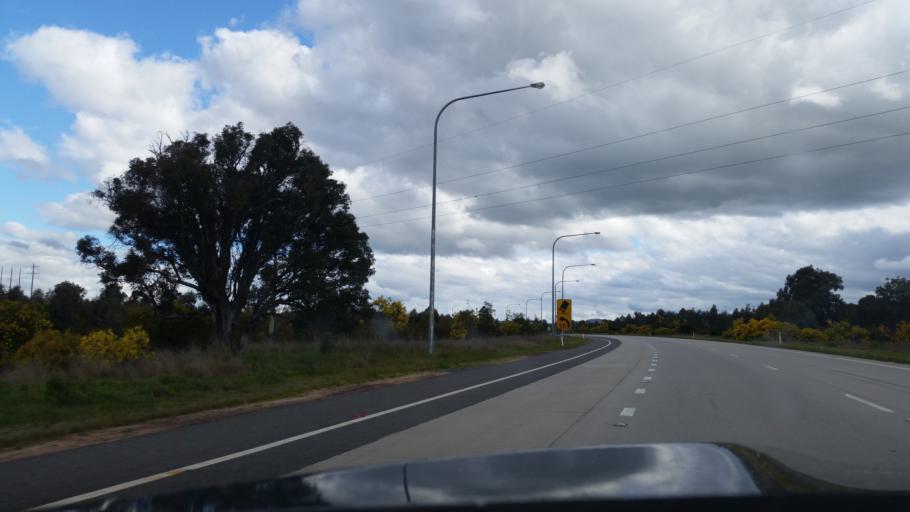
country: AU
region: New South Wales
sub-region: Greater Hume Shire
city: Jindera
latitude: -35.9277
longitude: 147.0060
